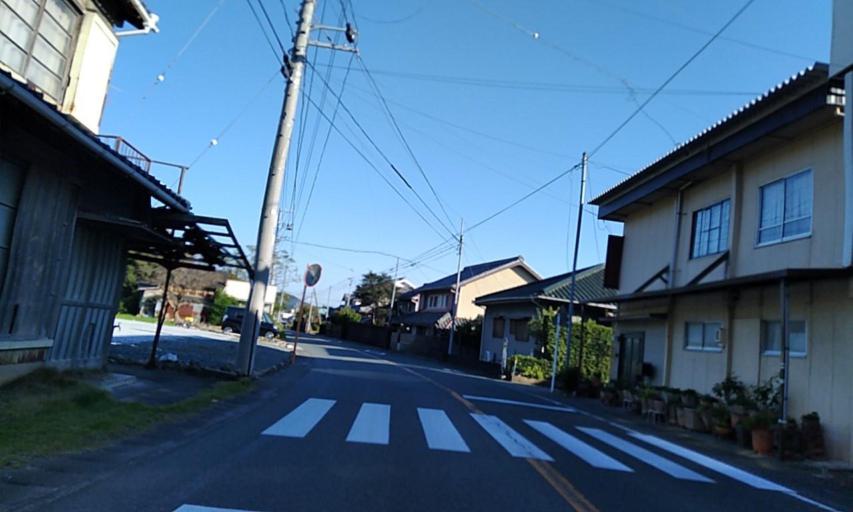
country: JP
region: Shizuoka
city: Hamakita
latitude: 34.8366
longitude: 137.6562
